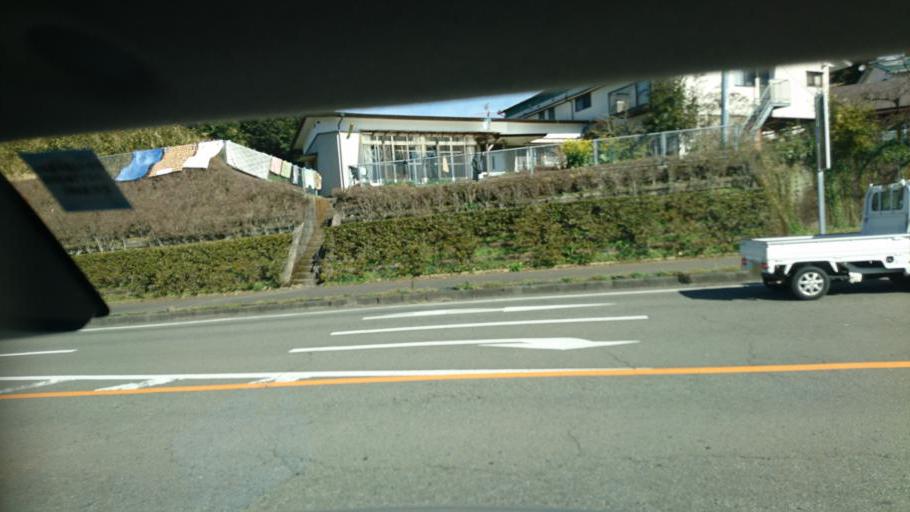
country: JP
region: Oita
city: Takedamachi
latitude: 32.6832
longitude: 131.3505
